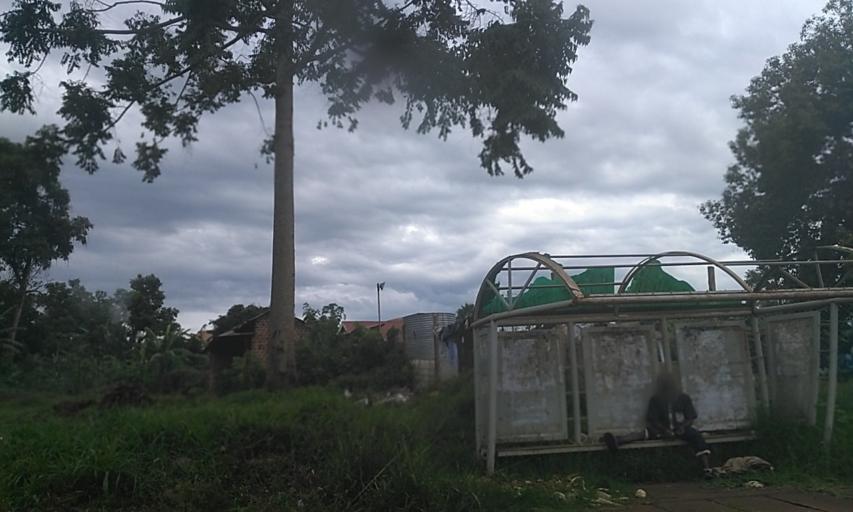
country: UG
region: Central Region
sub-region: Wakiso District
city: Bweyogerere
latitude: 0.3933
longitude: 32.6622
